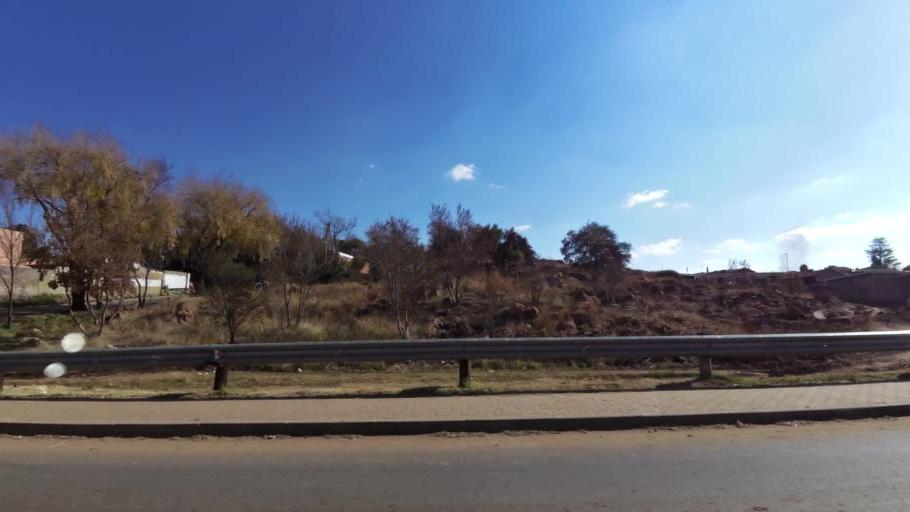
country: ZA
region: Gauteng
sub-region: City of Johannesburg Metropolitan Municipality
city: Soweto
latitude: -26.2421
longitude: 27.9099
